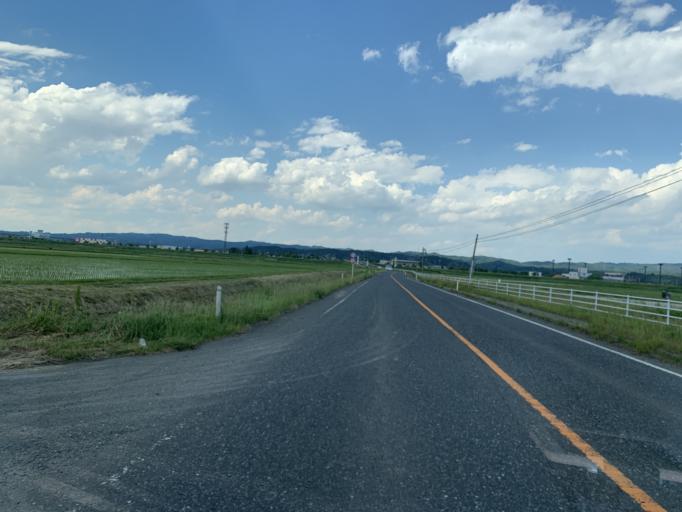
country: JP
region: Miyagi
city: Wakuya
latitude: 38.5253
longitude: 141.1307
